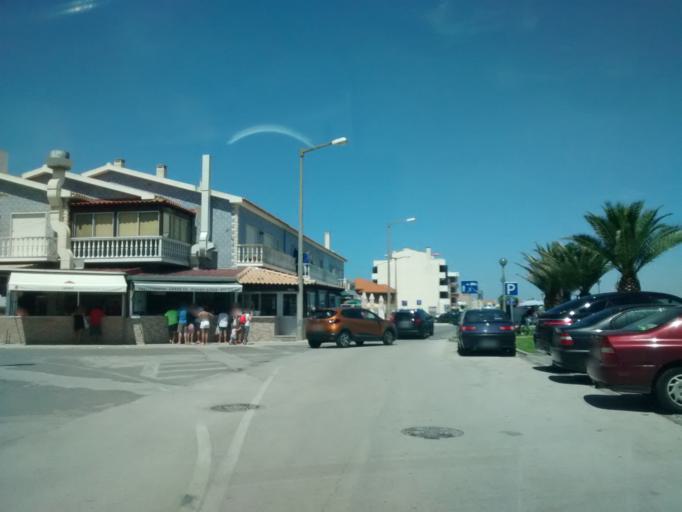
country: PT
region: Coimbra
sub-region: Mira
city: Mira
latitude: 40.4516
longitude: -8.8018
